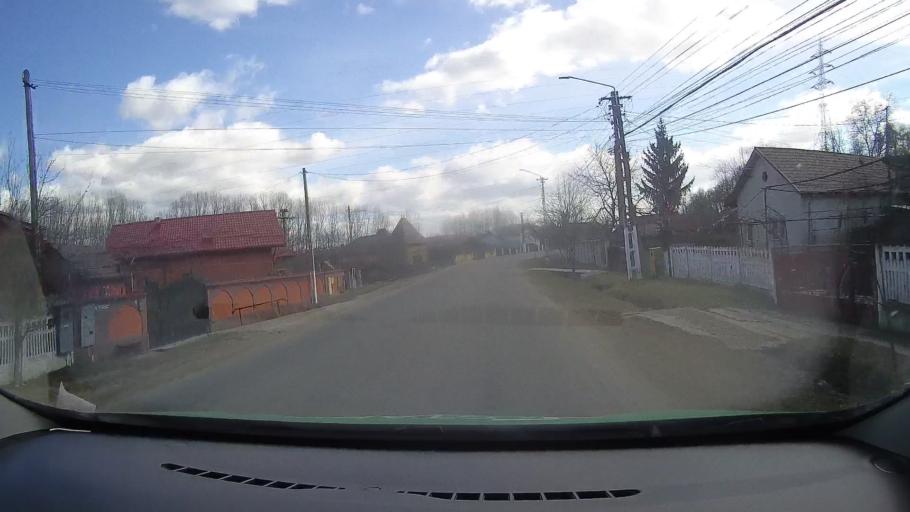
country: RO
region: Dambovita
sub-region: Comuna Doicesti
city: Doicesti
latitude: 44.9739
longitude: 25.3942
